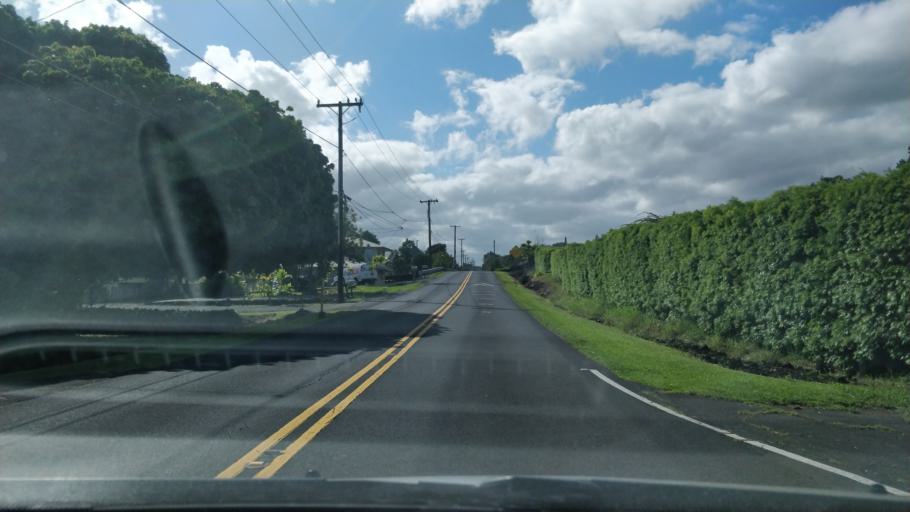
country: US
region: Hawaii
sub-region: Hawaii County
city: Hilo
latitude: 19.6796
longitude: -155.1063
